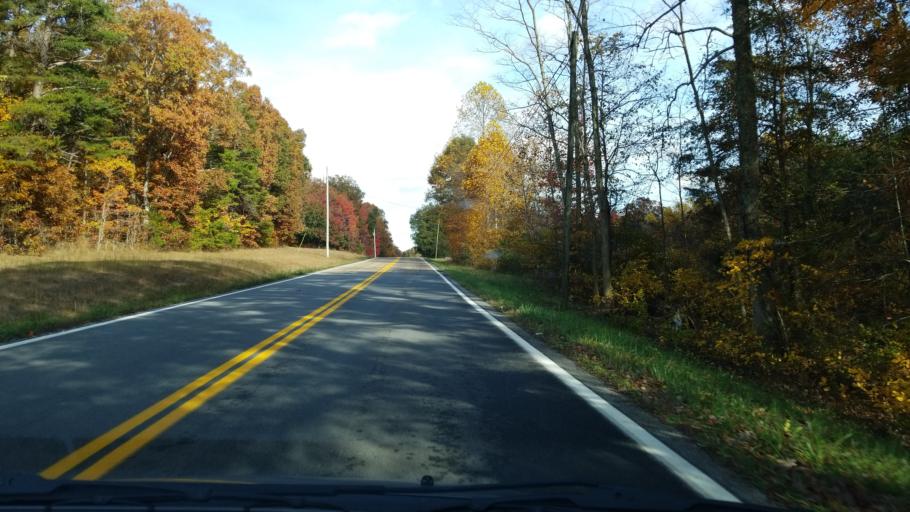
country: US
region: Tennessee
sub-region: Sequatchie County
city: Dunlap
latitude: 35.4661
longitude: -85.4781
